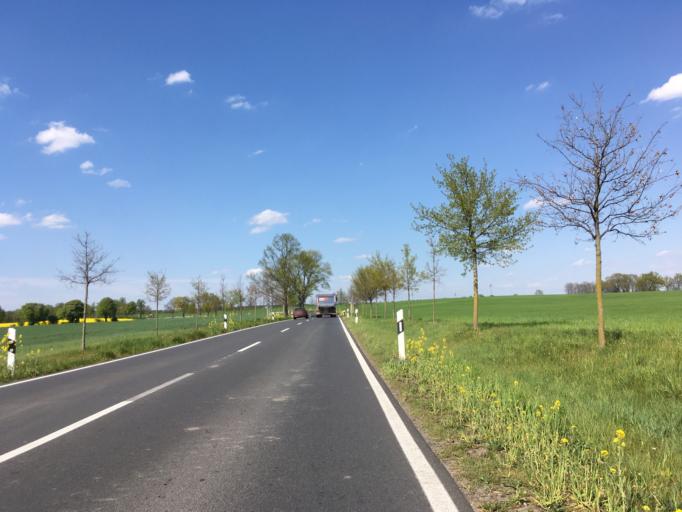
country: DE
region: Brandenburg
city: Ahrensfelde
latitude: 52.6096
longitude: 13.6183
